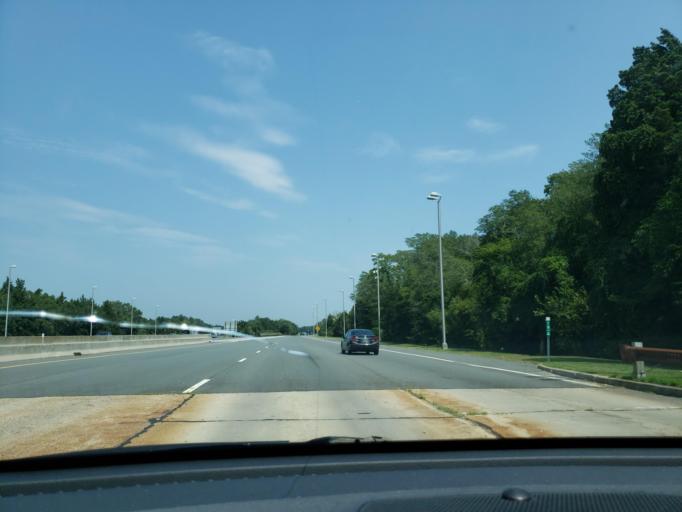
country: US
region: New Jersey
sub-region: Cape May County
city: Sea Isle City
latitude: 39.1938
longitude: -74.7097
